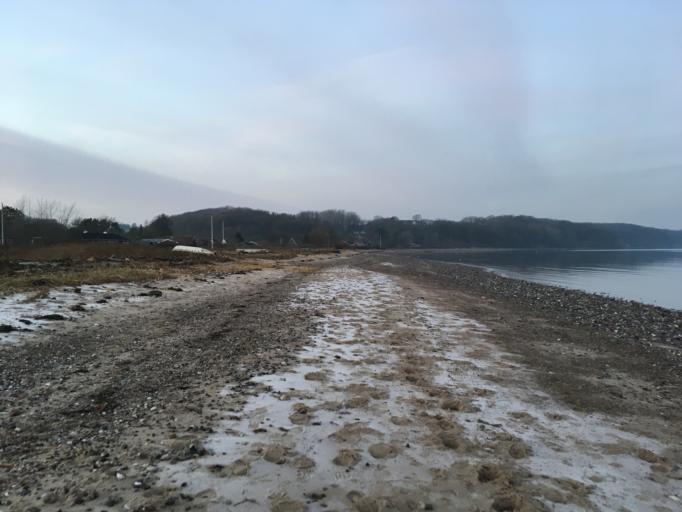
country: DK
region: South Denmark
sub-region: Middelfart Kommune
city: Norre Aby
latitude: 55.5217
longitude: 9.8523
